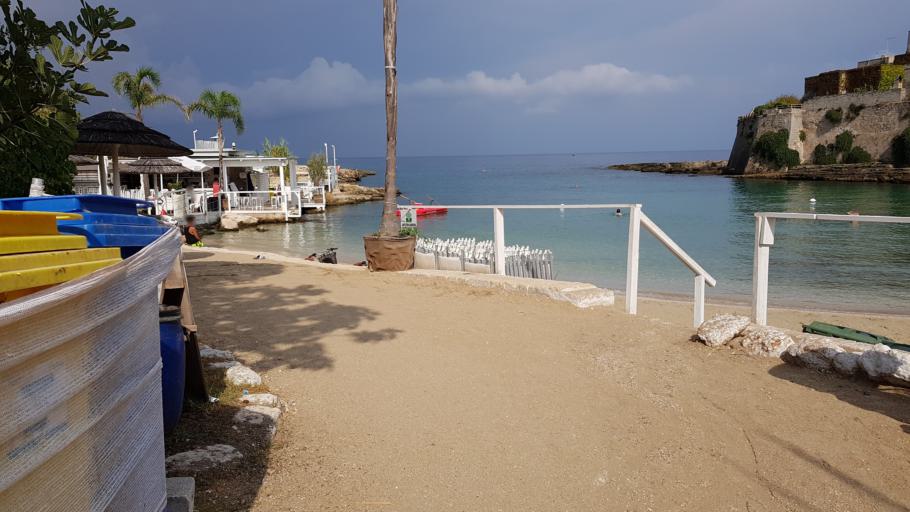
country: IT
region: Apulia
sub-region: Provincia di Bari
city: Monopoli
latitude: 40.9298
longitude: 17.3308
